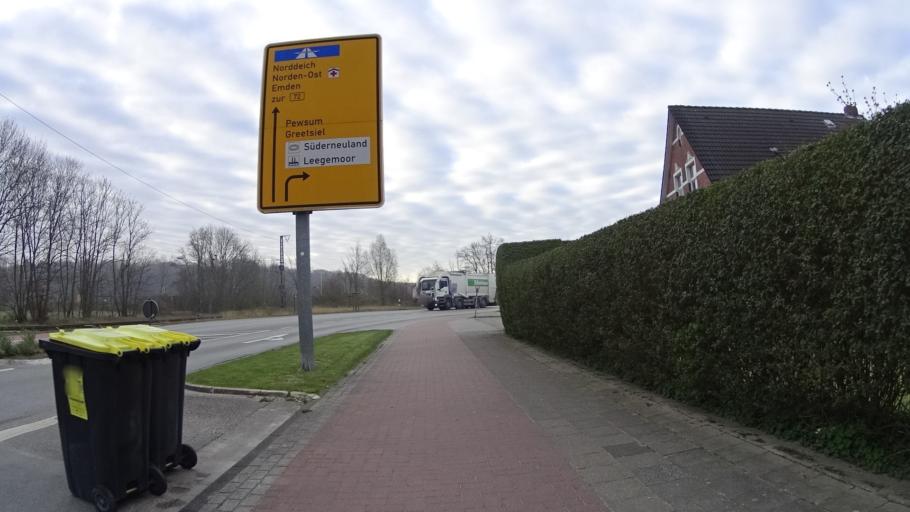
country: DE
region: Lower Saxony
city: Norden
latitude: 53.5840
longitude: 7.2249
